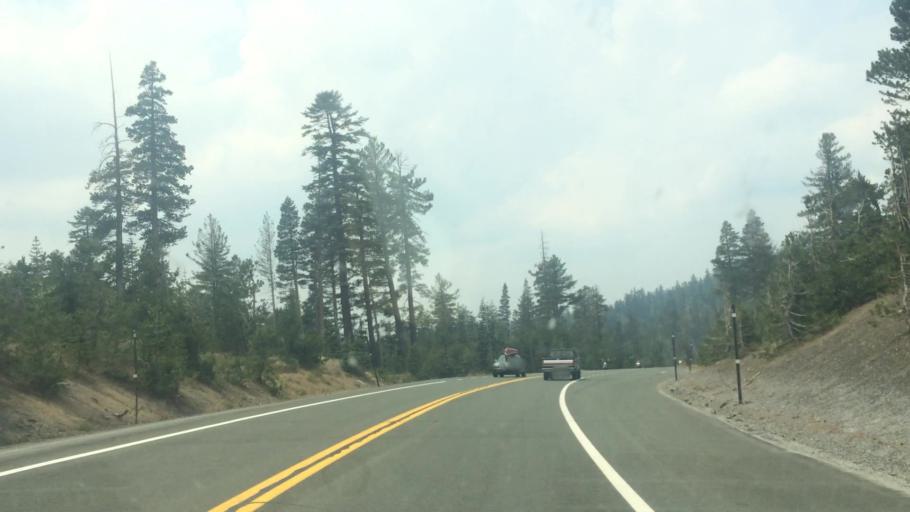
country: US
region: California
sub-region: El Dorado County
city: South Lake Tahoe
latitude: 38.6375
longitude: -120.1410
